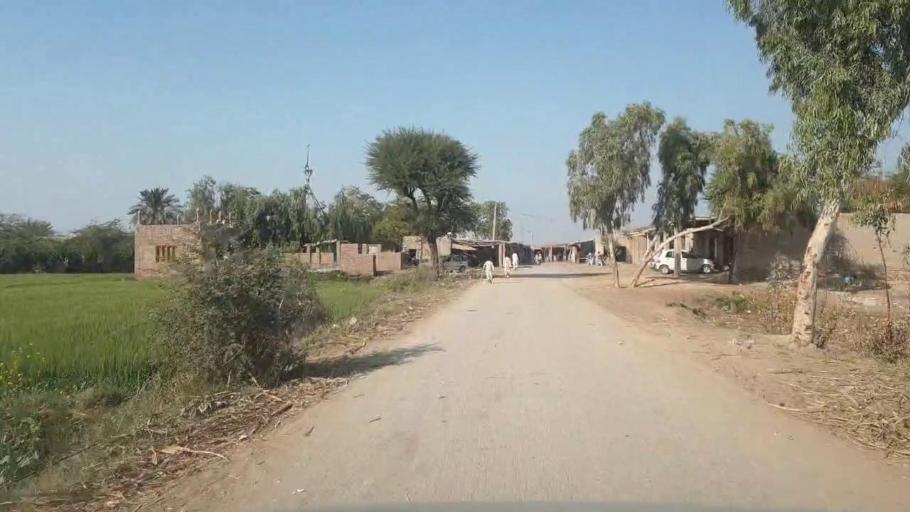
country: PK
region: Sindh
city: Chambar
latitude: 25.2930
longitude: 68.8637
